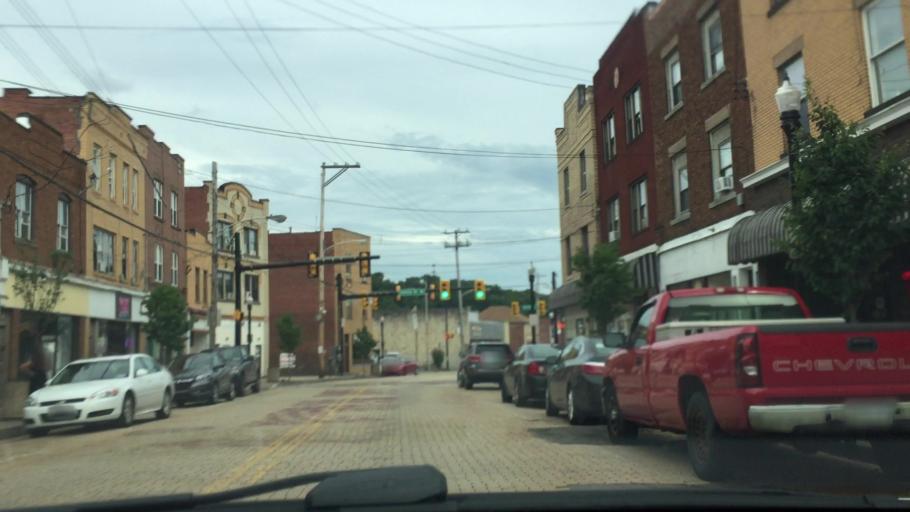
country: US
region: Pennsylvania
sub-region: Allegheny County
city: McKees Rocks
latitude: 40.4727
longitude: -80.0740
